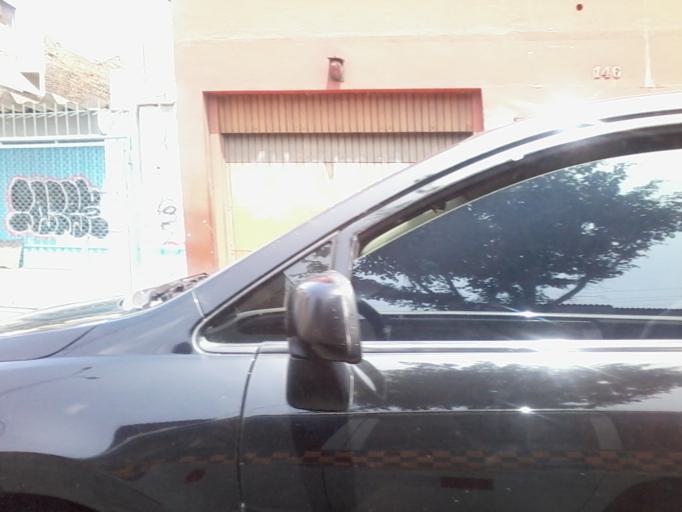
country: PE
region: Lima
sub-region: Lima
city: San Isidro
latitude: -12.0837
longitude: -77.0353
